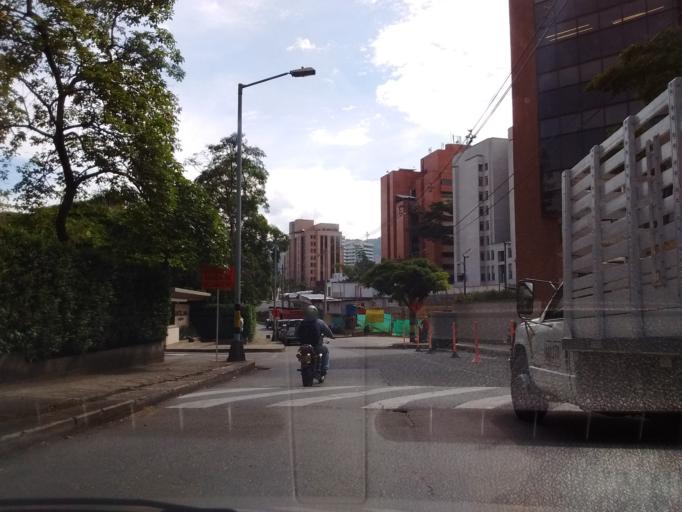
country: CO
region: Antioquia
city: Itagui
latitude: 6.2020
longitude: -75.5735
